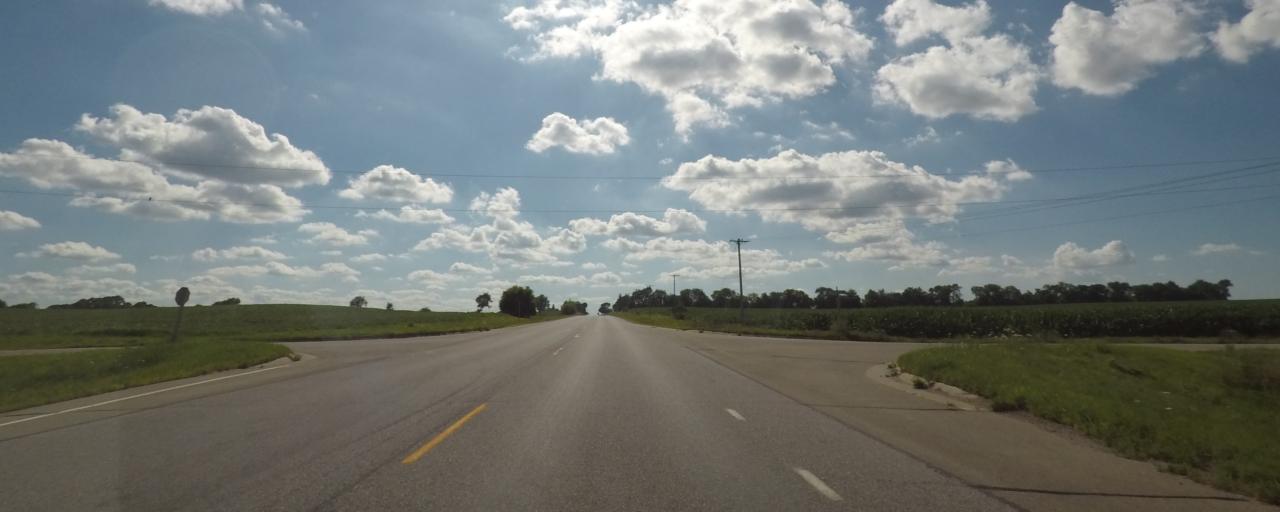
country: US
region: Wisconsin
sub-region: Dane County
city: Stoughton
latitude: 42.9198
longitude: -89.1314
